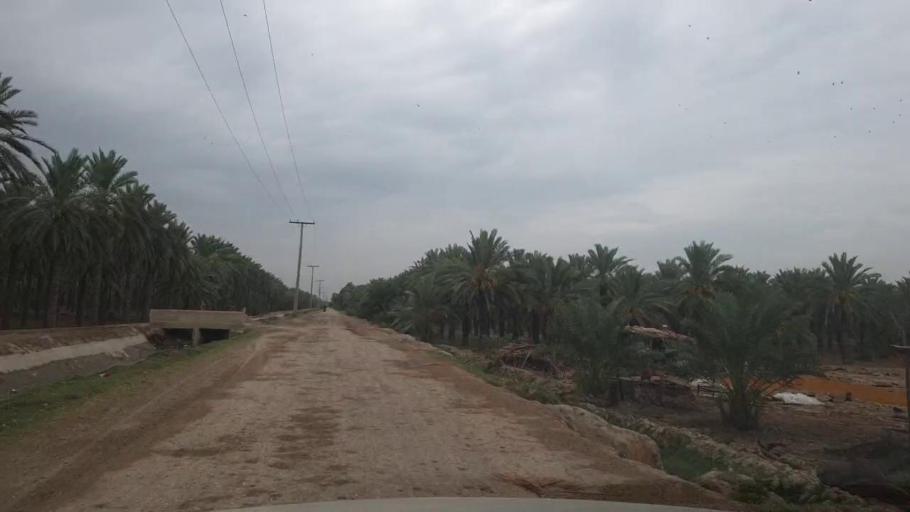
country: PK
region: Sindh
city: Khairpur
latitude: 27.6114
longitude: 68.8175
